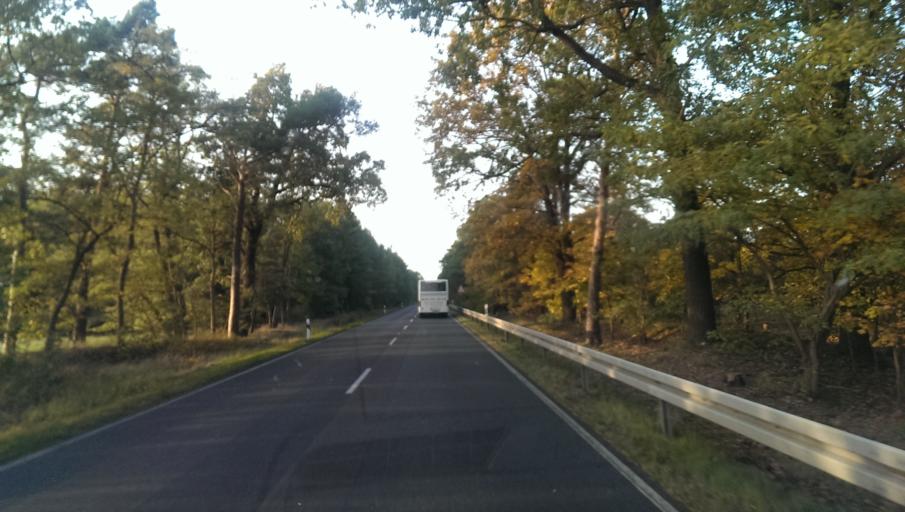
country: DE
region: Saxony-Anhalt
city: Holzdorf
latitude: 51.7633
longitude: 13.2036
